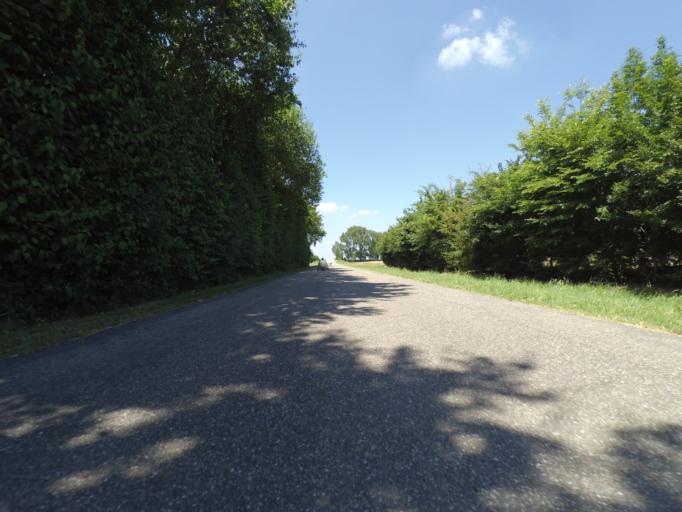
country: NL
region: Zeeland
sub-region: Gemeente Reimerswaal
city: Yerseke
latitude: 51.5601
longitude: 4.0570
